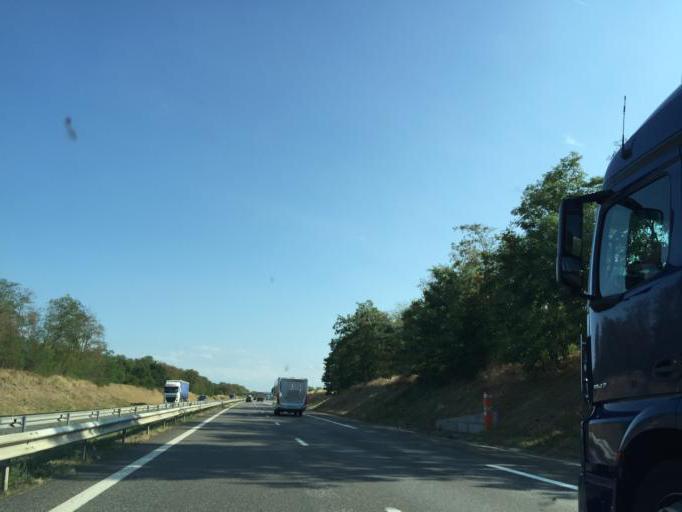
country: FR
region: Rhone-Alpes
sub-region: Departement de la Loire
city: Cuzieu
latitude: 45.6044
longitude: 4.2088
